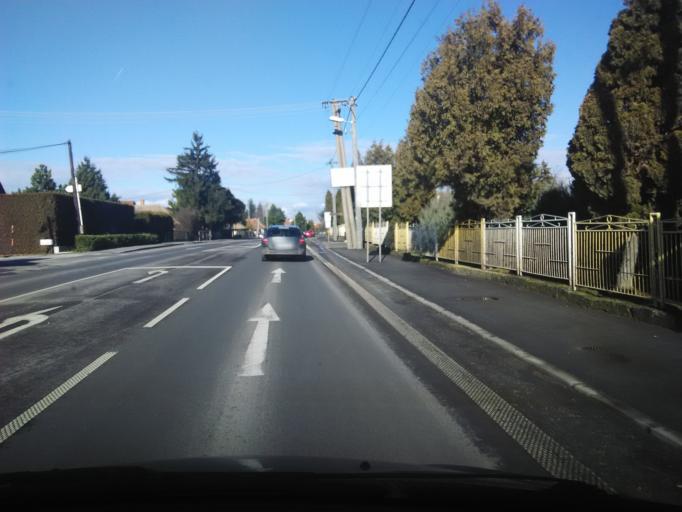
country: SK
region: Nitriansky
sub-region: Okres Nitra
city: Nitra
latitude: 48.2444
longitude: 18.1131
